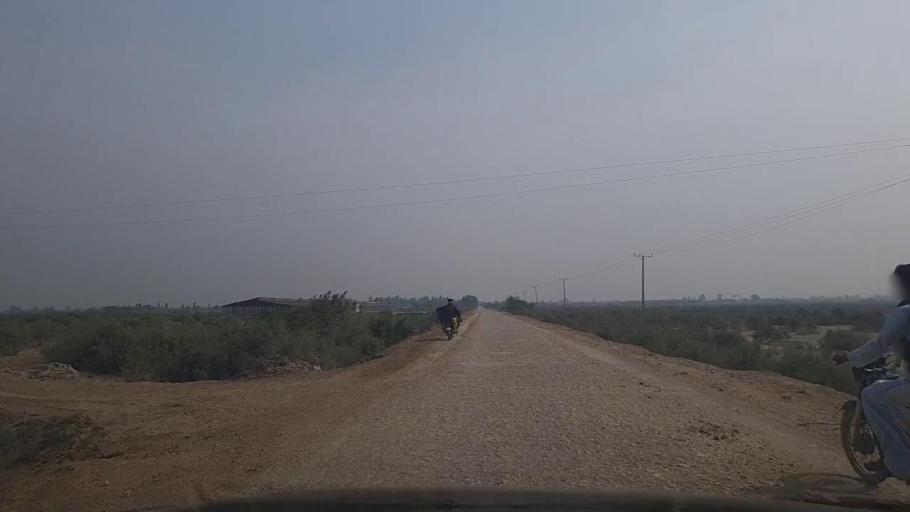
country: PK
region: Sindh
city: Mirpur Sakro
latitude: 24.4573
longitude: 67.7009
